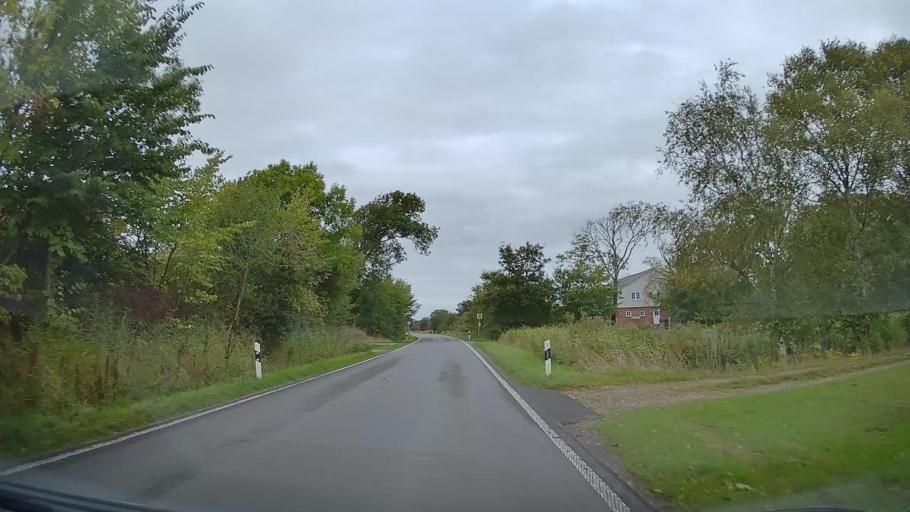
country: DE
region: Schleswig-Holstein
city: Klanxbull
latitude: 54.8708
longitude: 8.6814
